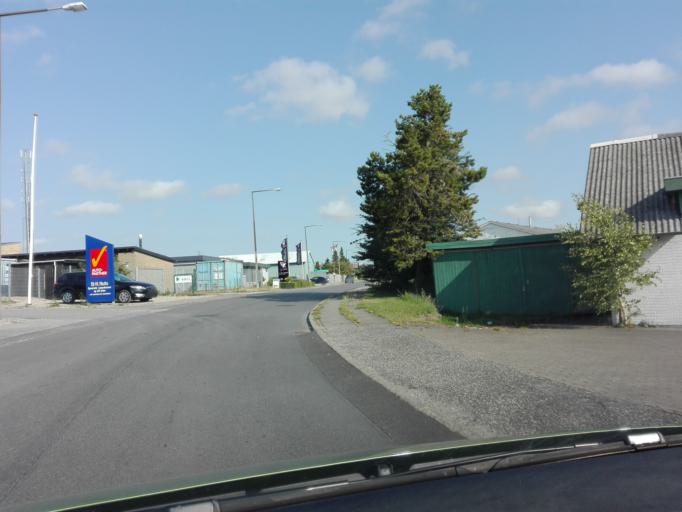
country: DK
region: Central Jutland
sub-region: Arhus Kommune
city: Lystrup
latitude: 56.2026
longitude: 10.2326
